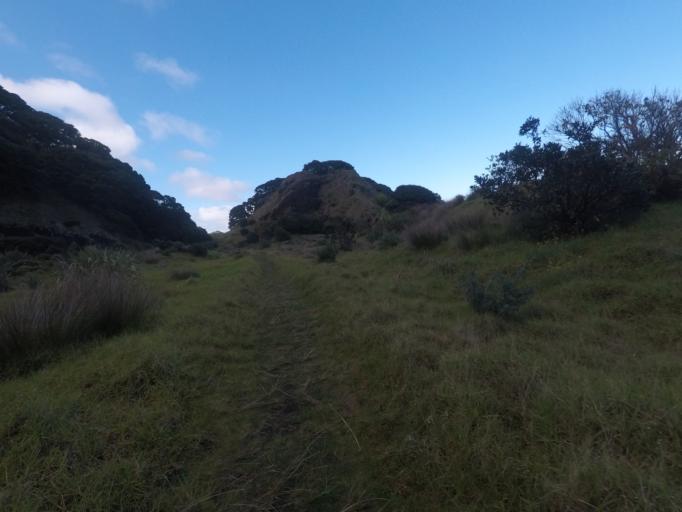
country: NZ
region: Auckland
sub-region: Auckland
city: Titirangi
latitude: -37.0018
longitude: 174.4803
